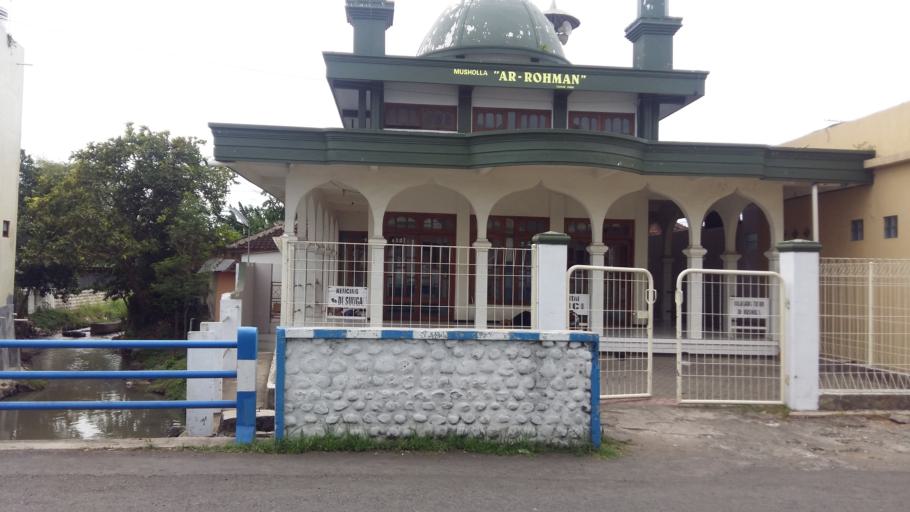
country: ID
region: East Java
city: Krajan
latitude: -8.3055
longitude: 114.2926
